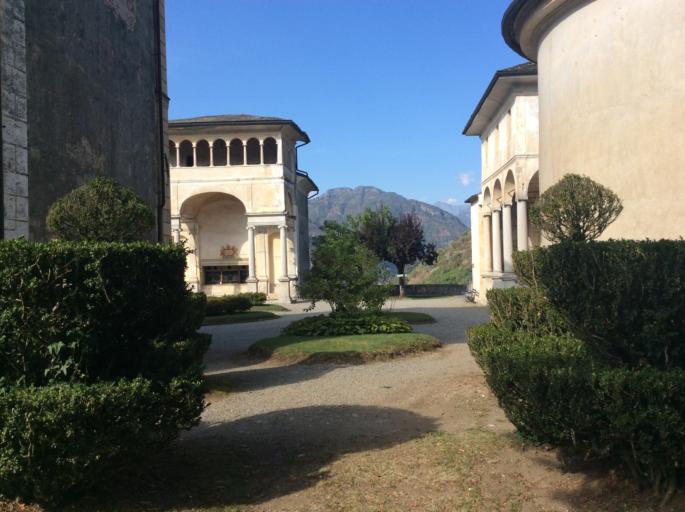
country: IT
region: Piedmont
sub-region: Provincia di Vercelli
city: Varallo
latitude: 45.8191
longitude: 8.2557
